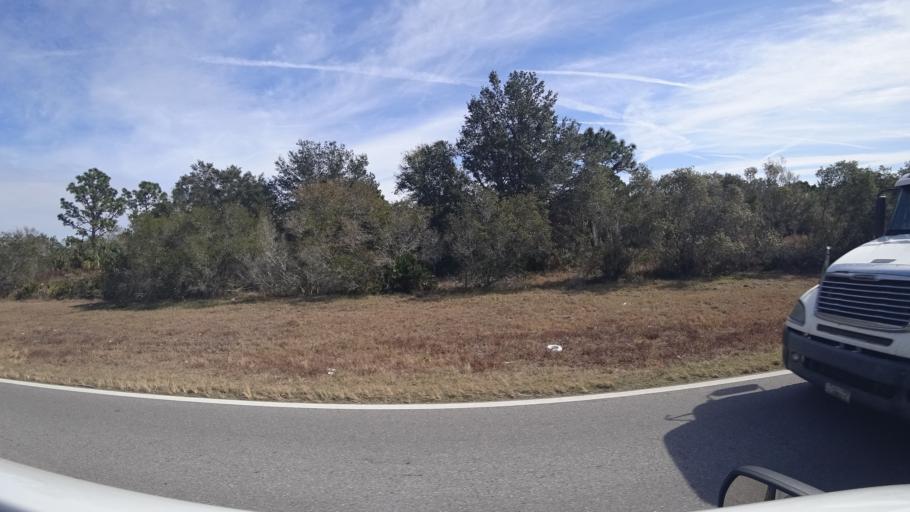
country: US
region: Florida
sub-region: Manatee County
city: Ellenton
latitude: 27.5302
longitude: -82.3685
